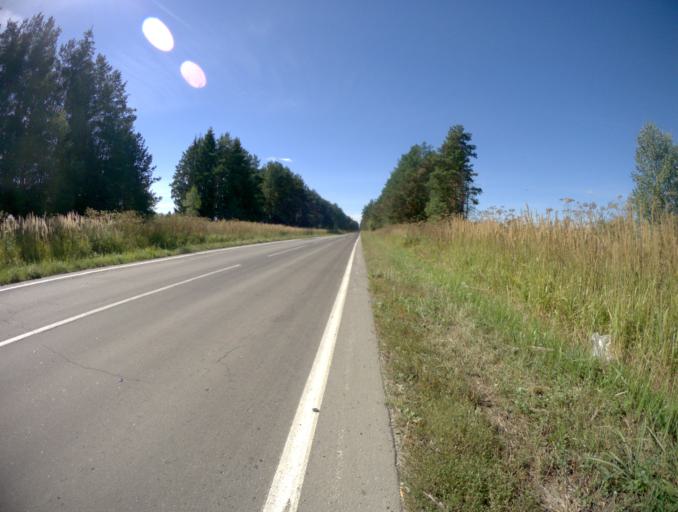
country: RU
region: Vladimir
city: Zolotkovo
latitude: 55.6198
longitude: 41.0504
